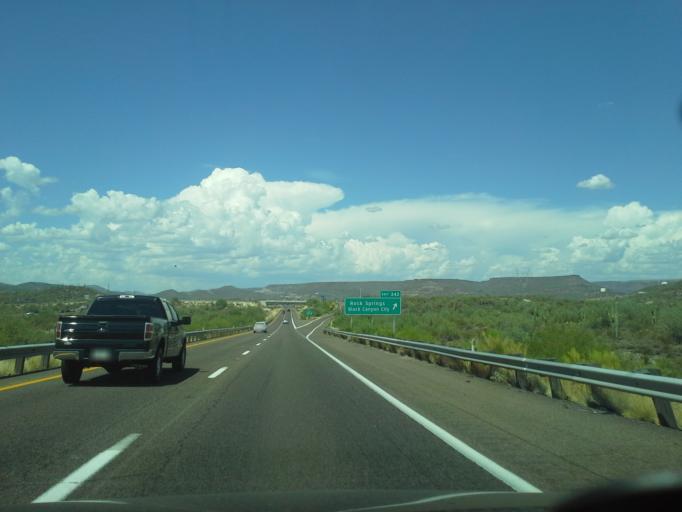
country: US
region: Arizona
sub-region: Yavapai County
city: Black Canyon City
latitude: 34.0489
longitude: -112.1455
